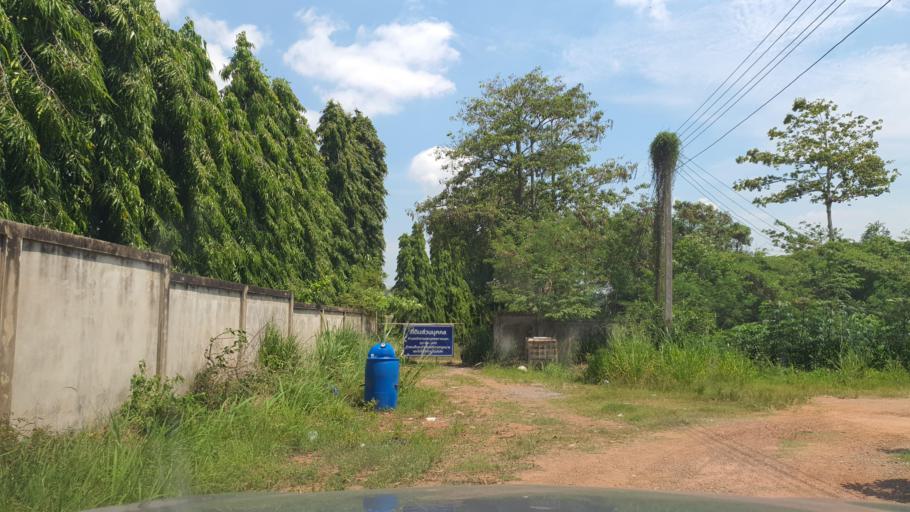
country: TH
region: Rayong
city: Ban Chang
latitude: 12.7624
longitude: 100.9604
